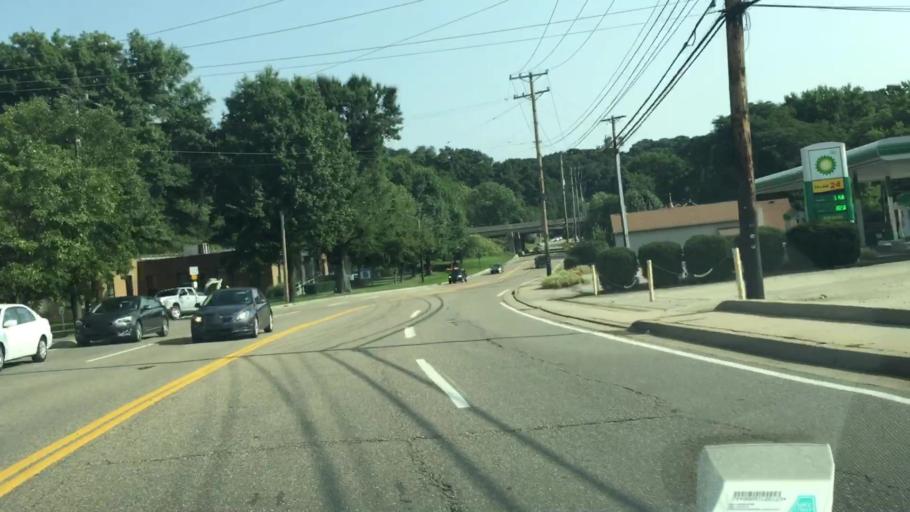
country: US
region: Pennsylvania
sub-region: Allegheny County
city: Aspinwall
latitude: 40.4889
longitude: -79.8831
